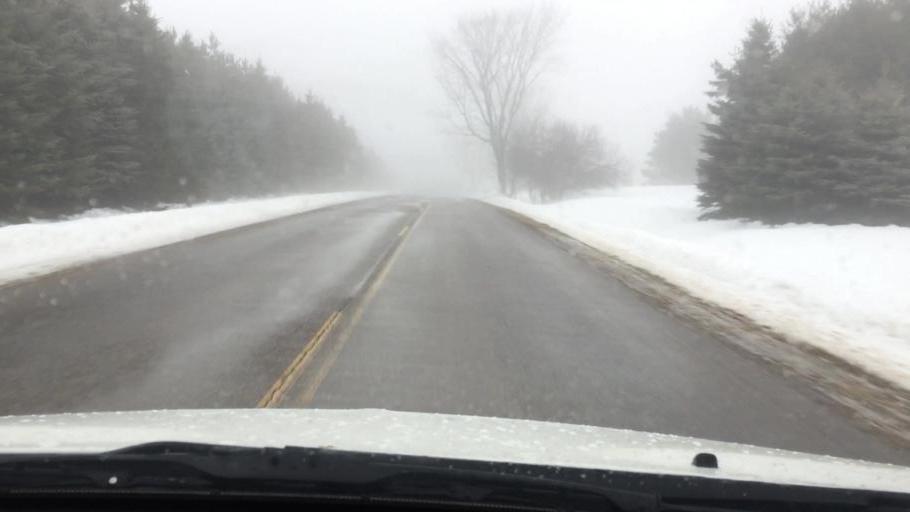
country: US
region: Michigan
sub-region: Charlevoix County
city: East Jordan
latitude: 45.1213
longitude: -85.1802
